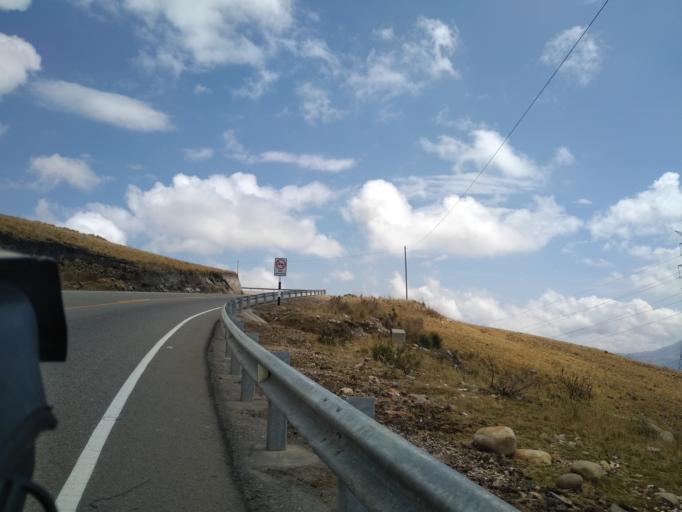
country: PE
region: La Libertad
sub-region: Provincia de Santiago de Chuco
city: Quiruvilca
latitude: -7.9223
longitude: -78.1550
